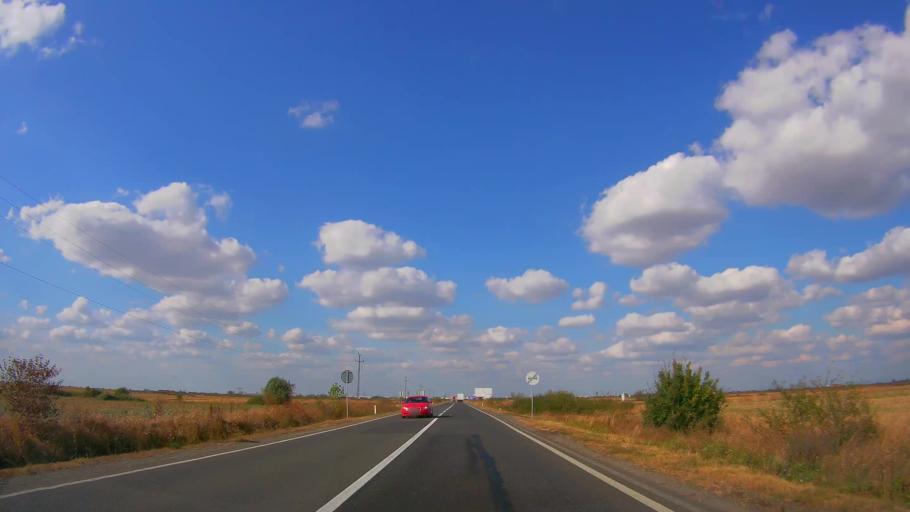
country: RO
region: Satu Mare
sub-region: Oras Ardud
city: Madaras
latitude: 47.7097
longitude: 22.8723
